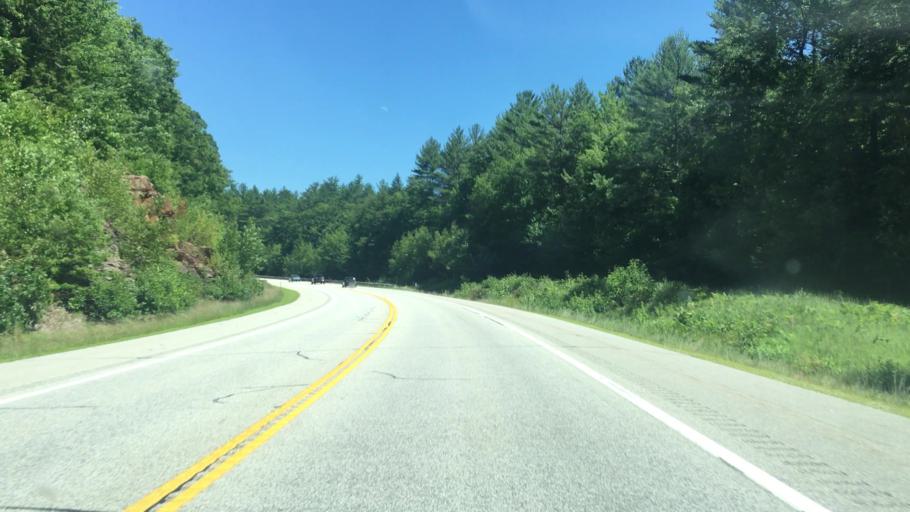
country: US
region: New Hampshire
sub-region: Merrimack County
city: Contoocook
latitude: 43.1769
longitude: -71.7274
